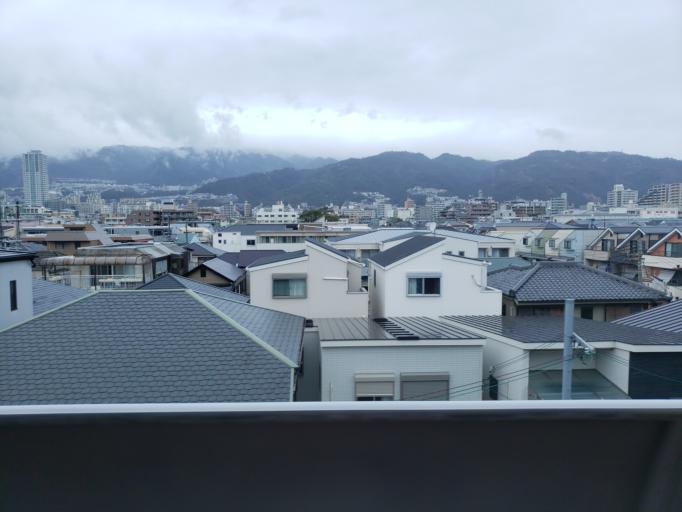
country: JP
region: Hyogo
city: Ashiya
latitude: 34.7140
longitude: 135.2752
